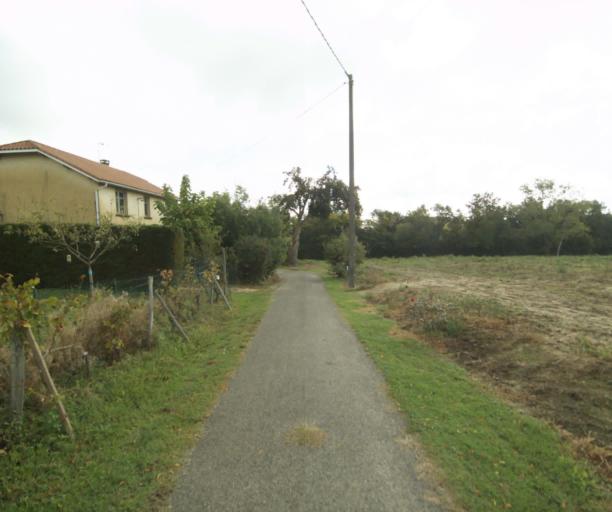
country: FR
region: Midi-Pyrenees
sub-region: Departement du Gers
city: Nogaro
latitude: 43.8382
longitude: -0.0759
